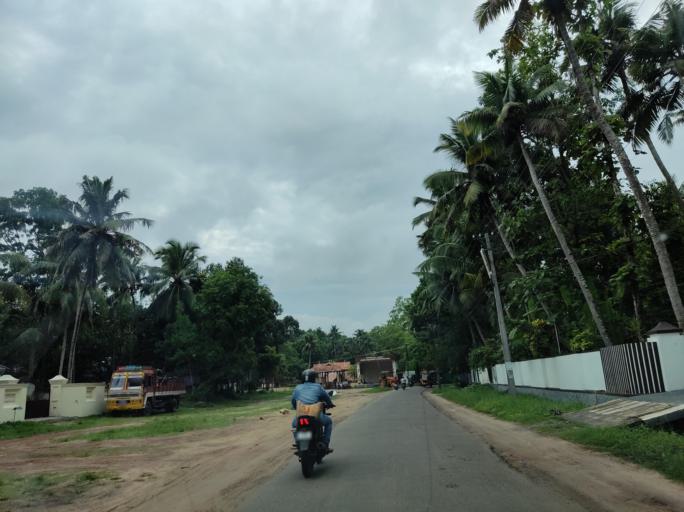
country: IN
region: Kerala
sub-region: Alappuzha
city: Mavelikara
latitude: 9.2415
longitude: 76.5241
